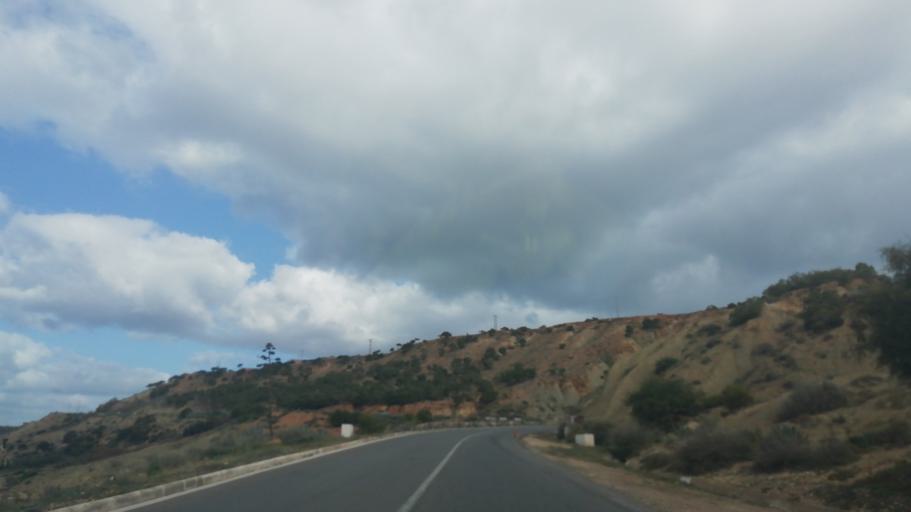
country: DZ
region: Relizane
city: Mazouna
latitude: 36.3053
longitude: 0.6712
